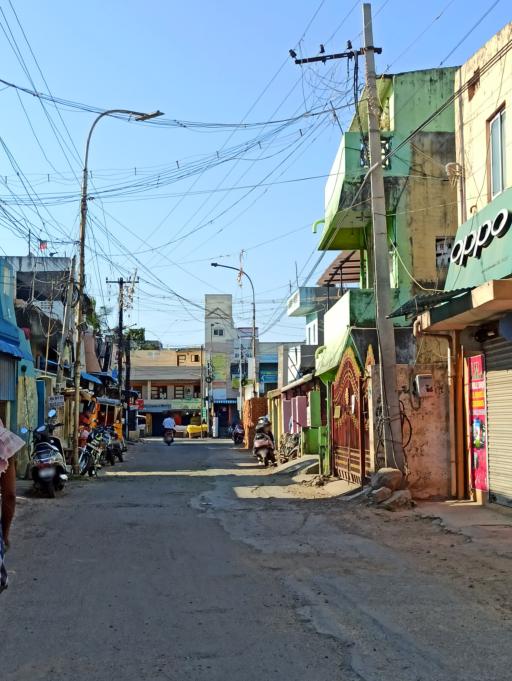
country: IN
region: Tamil Nadu
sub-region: Kancheepuram
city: Manappakkam
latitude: 13.0201
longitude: 80.1662
